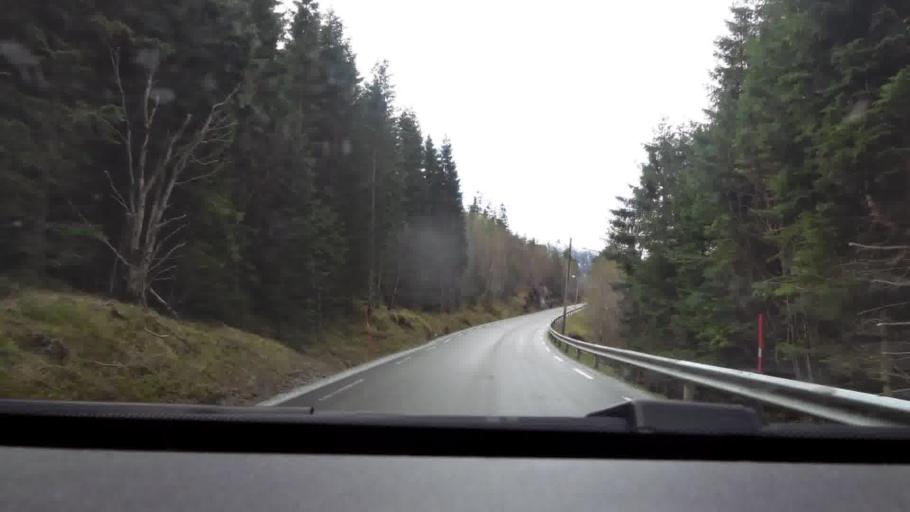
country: NO
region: More og Romsdal
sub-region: Eide
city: Eide
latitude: 62.9197
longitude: 7.5544
